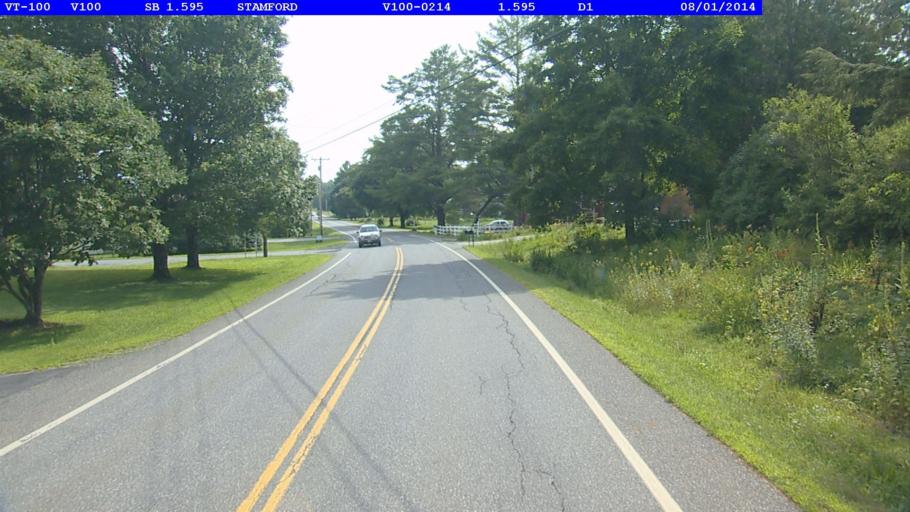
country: US
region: Massachusetts
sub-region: Berkshire County
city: North Adams
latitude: 42.7635
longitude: -73.0659
